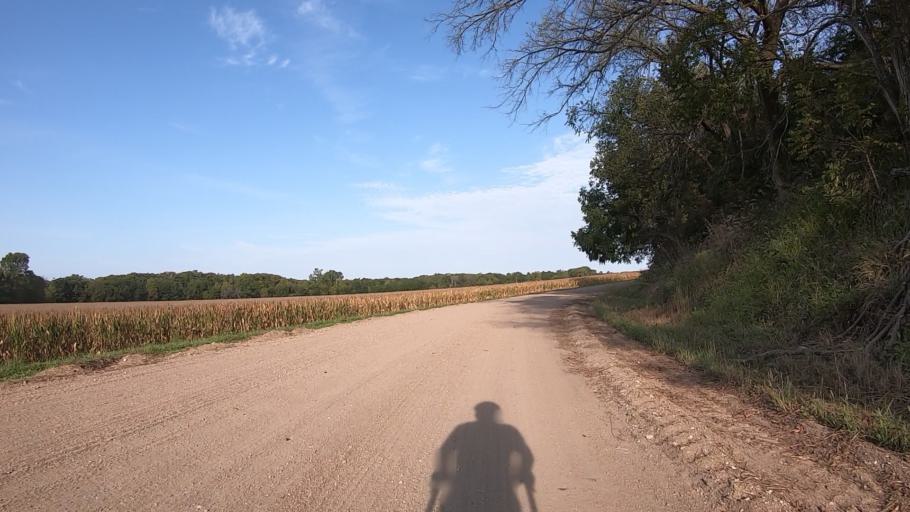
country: US
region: Kansas
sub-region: Marshall County
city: Blue Rapids
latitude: 39.6624
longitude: -96.8181
